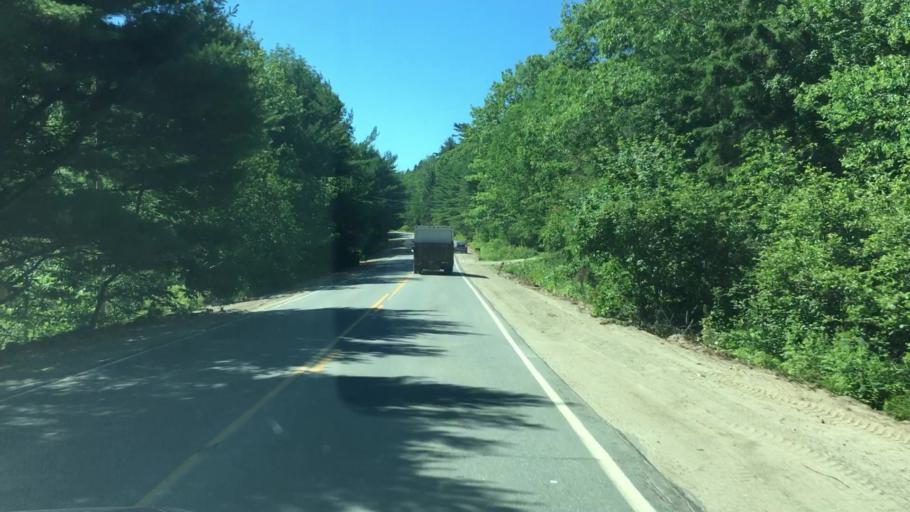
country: US
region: Maine
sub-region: Hancock County
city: Sedgwick
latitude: 44.3783
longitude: -68.5685
